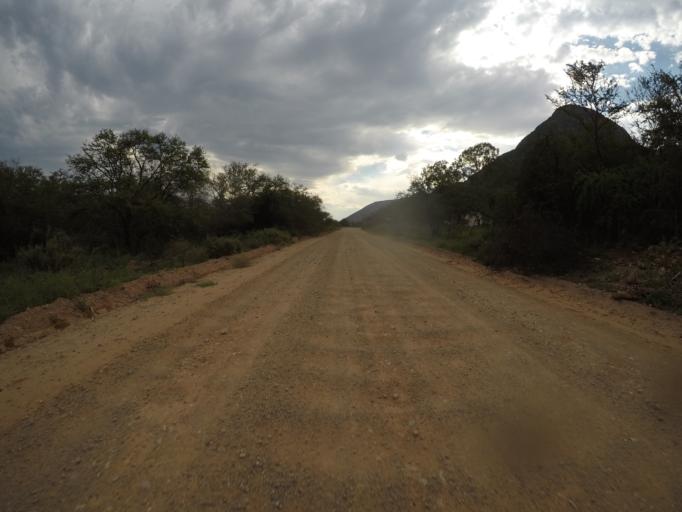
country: ZA
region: Eastern Cape
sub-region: Cacadu District Municipality
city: Kareedouw
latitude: -33.5790
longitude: 24.1484
